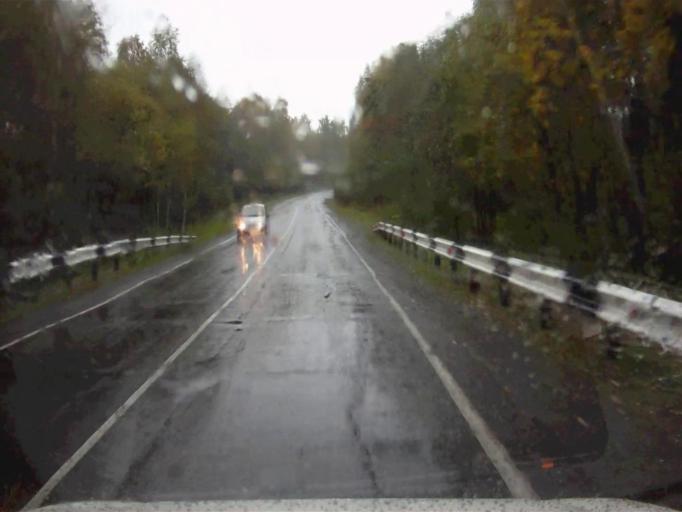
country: RU
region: Chelyabinsk
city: Kyshtym
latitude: 55.9106
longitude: 60.4342
